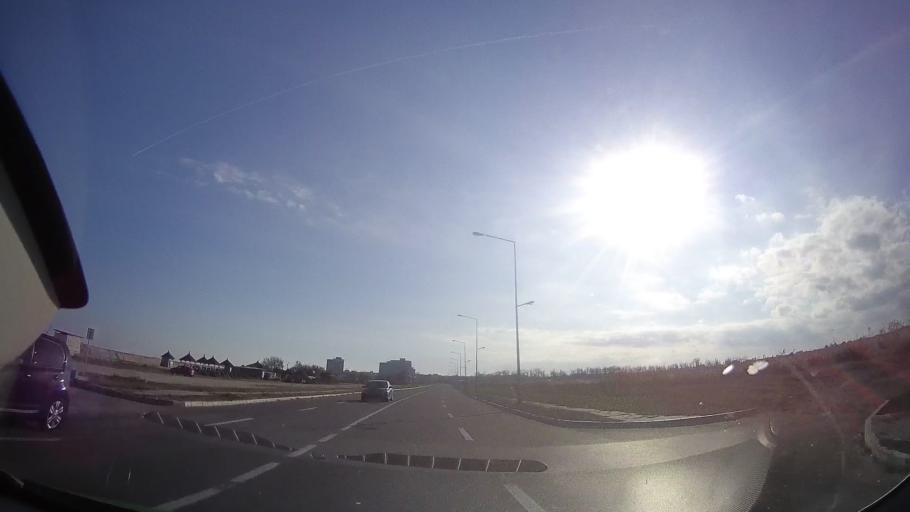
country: RO
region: Constanta
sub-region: Municipiul Mangalia
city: Mangalia
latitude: 43.8400
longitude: 28.5901
